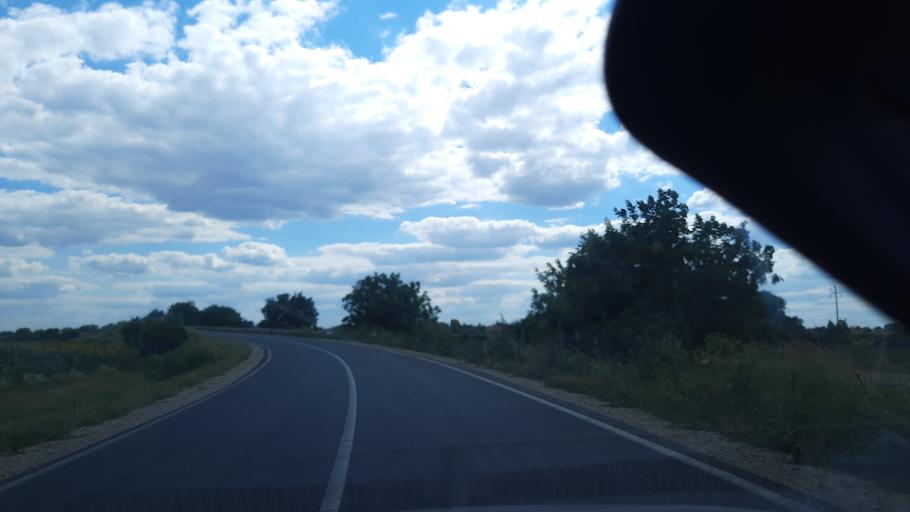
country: RS
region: Autonomna Pokrajina Vojvodina
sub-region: Sremski Okrug
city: Pecinci
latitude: 44.9191
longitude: 19.9738
